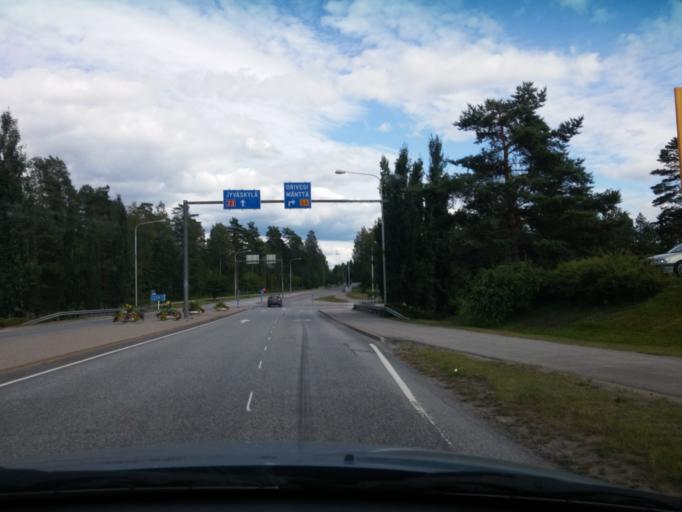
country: FI
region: Central Finland
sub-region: Keuruu
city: Keuruu
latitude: 62.2546
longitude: 24.7194
